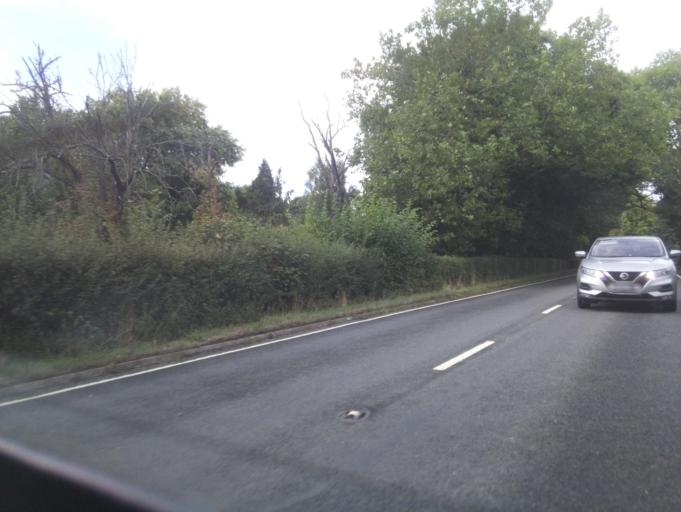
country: GB
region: England
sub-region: Worcestershire
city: Droitwich
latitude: 52.3174
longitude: -2.1766
